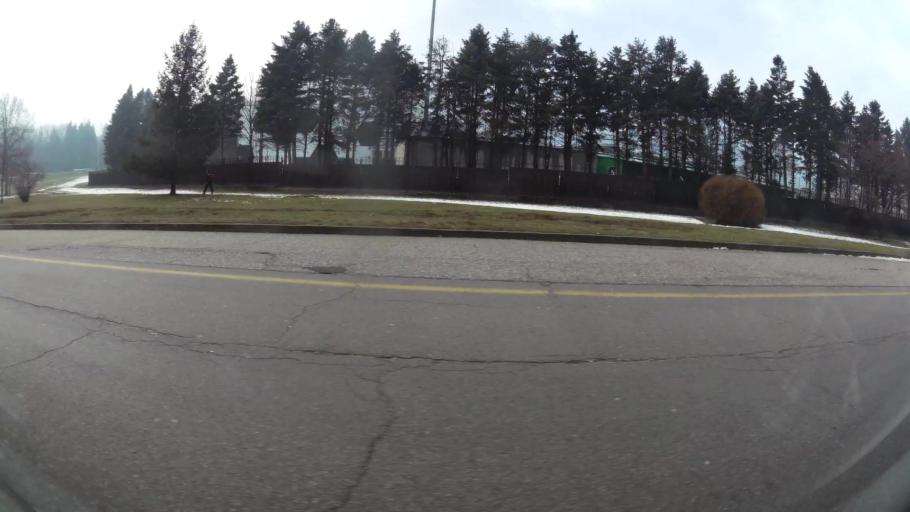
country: BG
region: Sofia-Capital
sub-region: Stolichna Obshtina
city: Sofia
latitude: 42.6537
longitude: 23.2804
